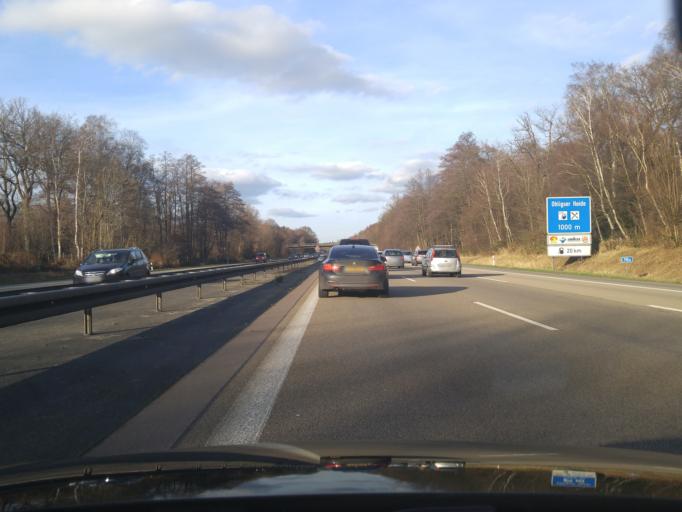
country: DE
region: North Rhine-Westphalia
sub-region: Regierungsbezirk Dusseldorf
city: Langenfeld
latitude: 51.1451
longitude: 6.9691
